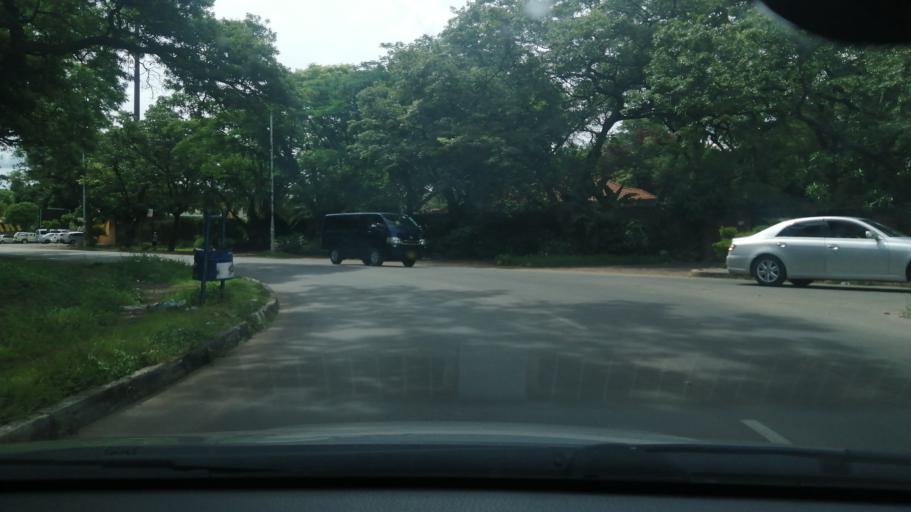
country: ZW
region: Harare
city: Harare
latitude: -17.8182
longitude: 31.0642
